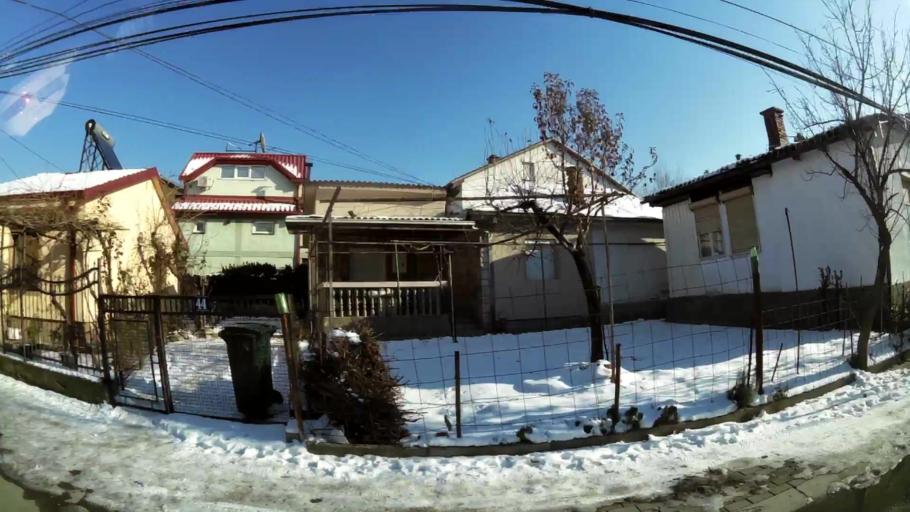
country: MK
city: Krushopek
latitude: 42.0028
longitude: 21.3804
